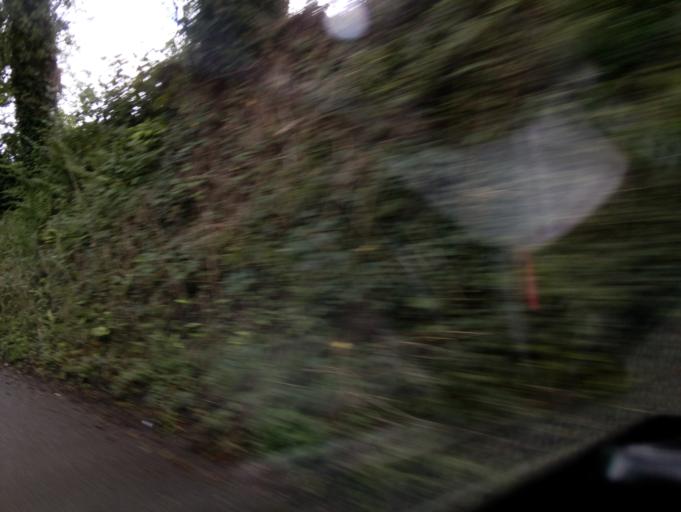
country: GB
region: England
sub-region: Devon
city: Modbury
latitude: 50.3285
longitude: -3.8429
